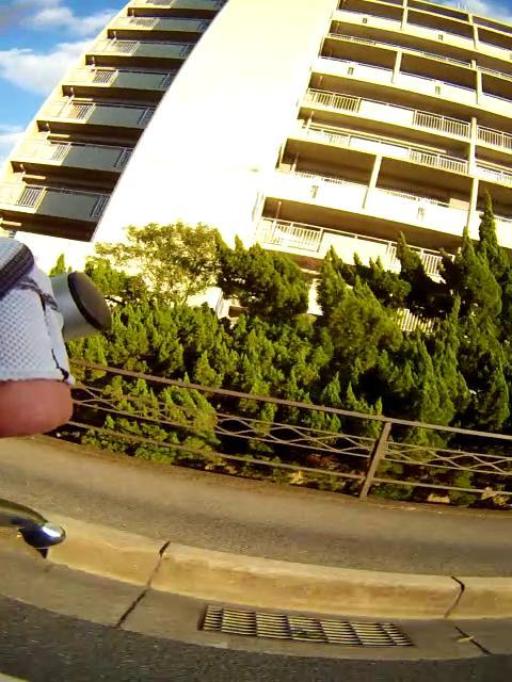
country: JP
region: Hyogo
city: Amagasaki
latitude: 34.7500
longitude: 135.4222
